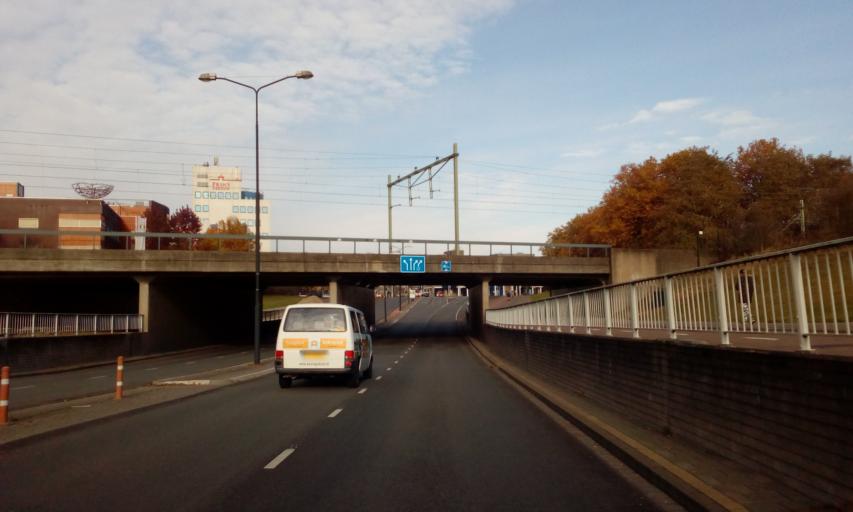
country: NL
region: Gelderland
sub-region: Gemeente Apeldoorn
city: Apeldoorn
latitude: 52.2072
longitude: 5.9581
